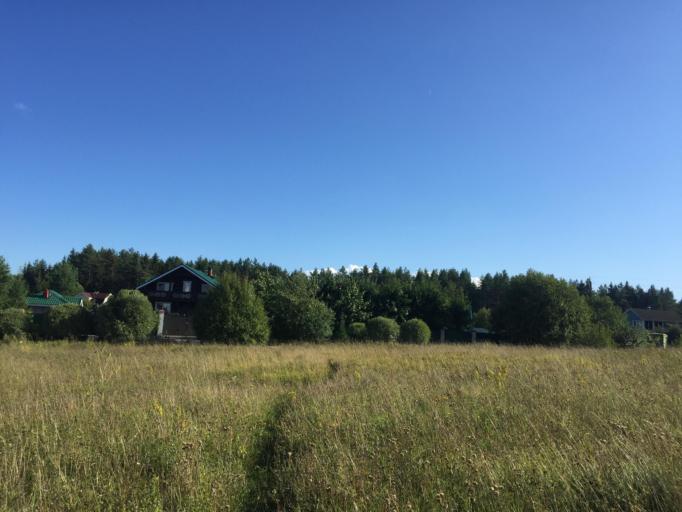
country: RU
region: Leningrad
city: Yelizavetino
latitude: 59.4193
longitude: 29.7717
